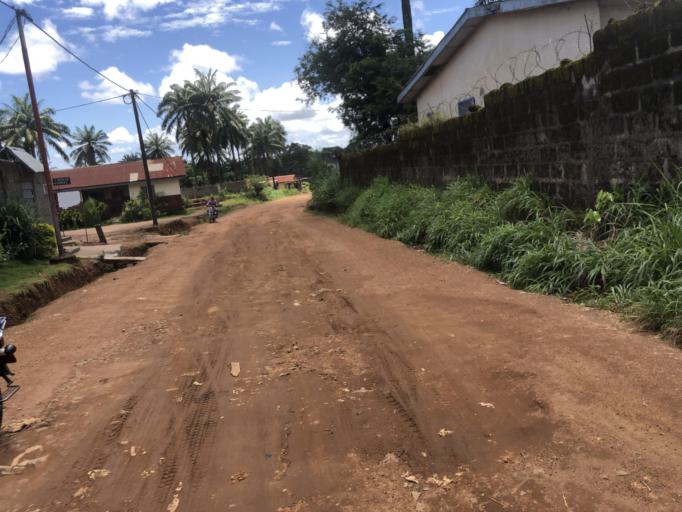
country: SL
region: Northern Province
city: Makeni
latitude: 8.8623
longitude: -12.0510
